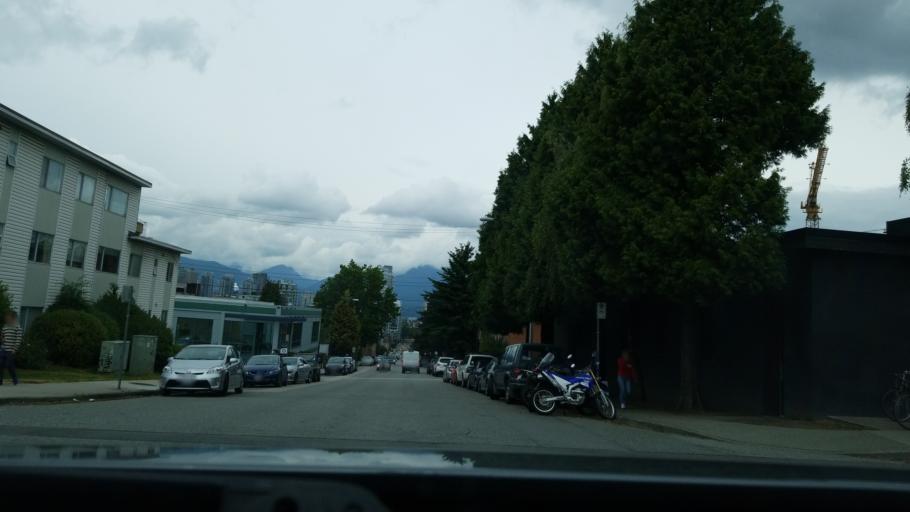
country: CA
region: British Columbia
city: Vancouver
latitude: 49.2637
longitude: -123.1030
